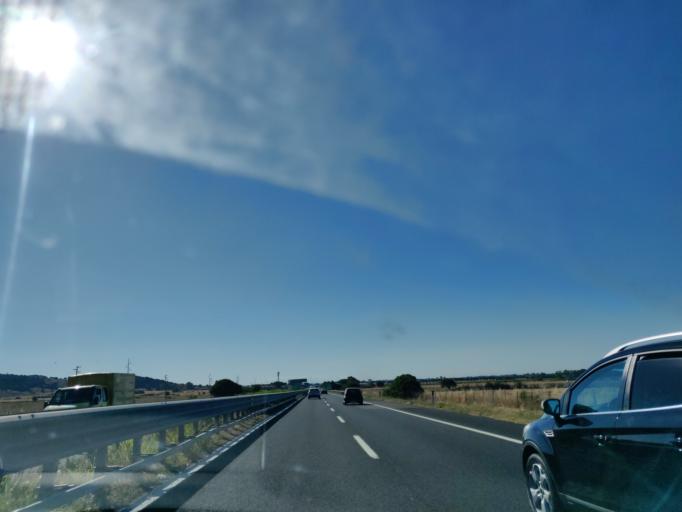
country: IT
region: Latium
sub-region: Citta metropolitana di Roma Capitale
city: Marina di Cerveteri
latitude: 42.0247
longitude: 11.9869
